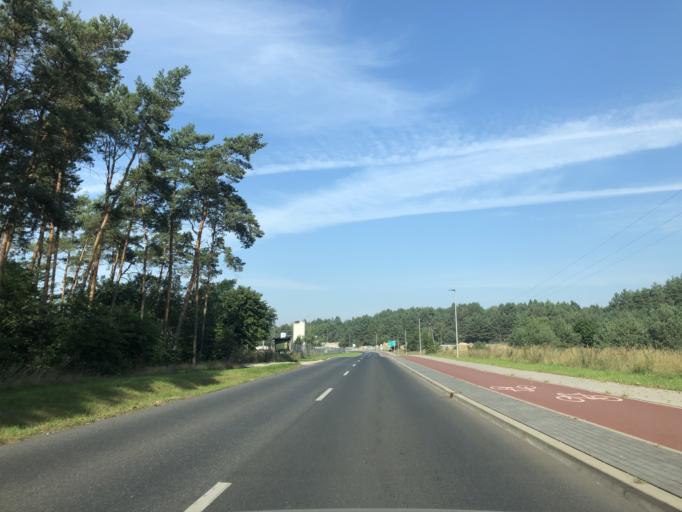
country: PL
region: Greater Poland Voivodeship
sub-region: Powiat pilski
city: Pila
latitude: 53.1387
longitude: 16.7908
